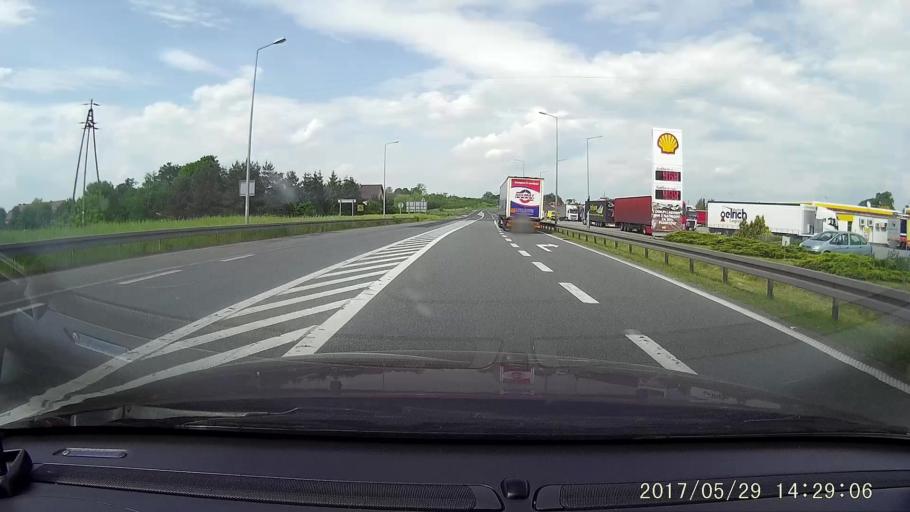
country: PL
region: Lower Silesian Voivodeship
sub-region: Powiat zgorzelecki
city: Lagow
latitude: 51.1763
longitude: 15.0309
